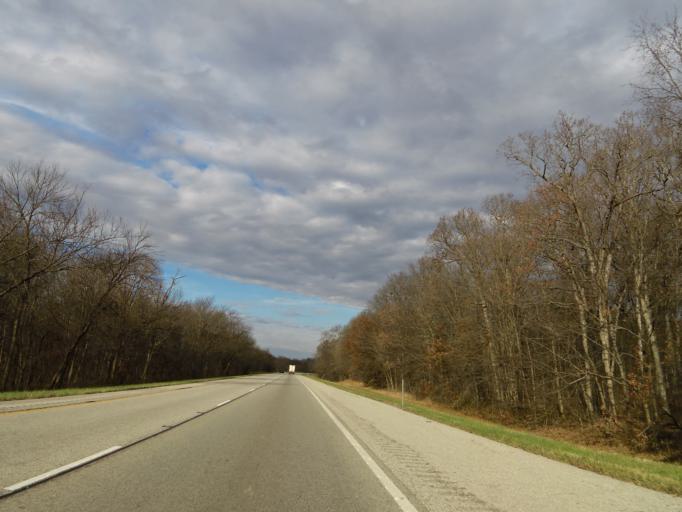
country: US
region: Illinois
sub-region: Washington County
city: Nashville
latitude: 38.4002
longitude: -89.3958
